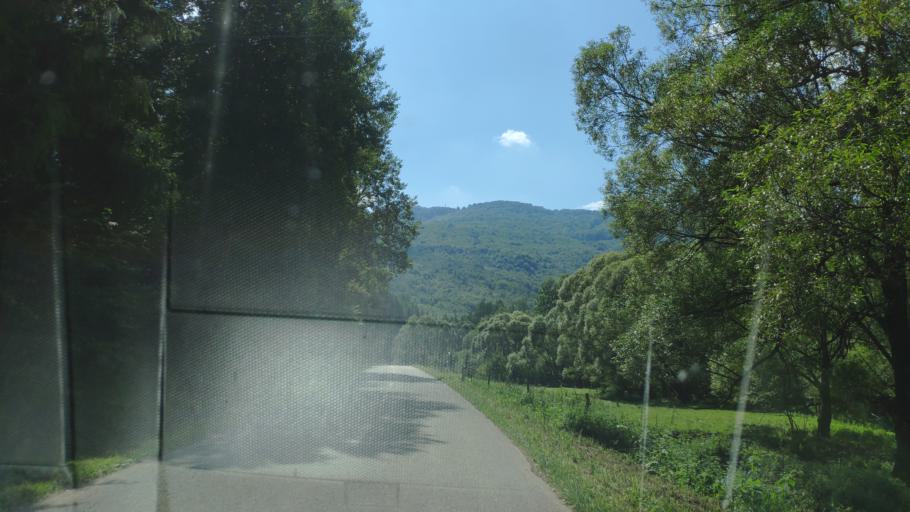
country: PL
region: Subcarpathian Voivodeship
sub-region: Powiat leski
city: Cisna
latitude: 49.0692
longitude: 22.3987
